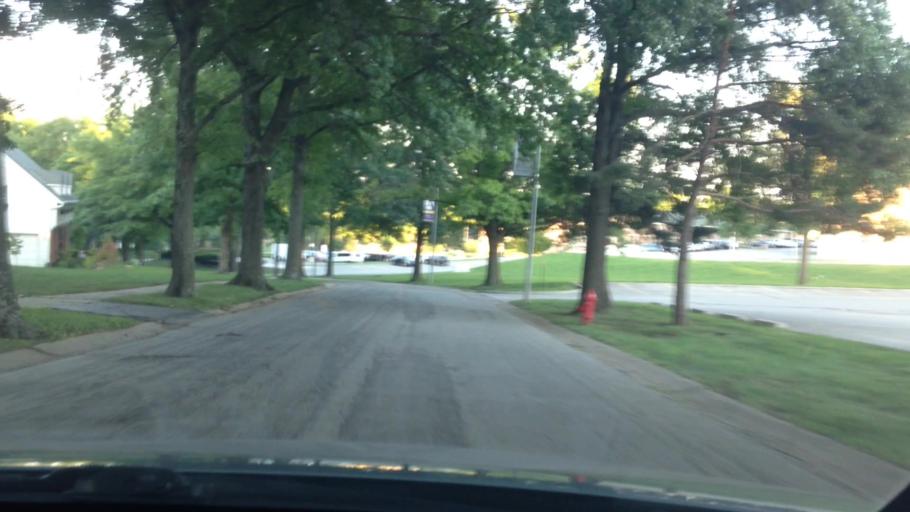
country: US
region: Kansas
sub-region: Johnson County
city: Leawood
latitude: 38.9142
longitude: -94.5928
